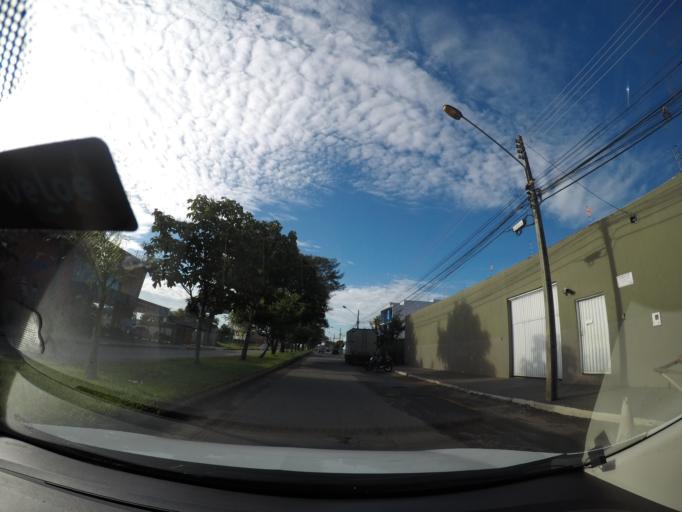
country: BR
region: Goias
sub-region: Goiania
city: Goiania
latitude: -16.7507
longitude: -49.2742
